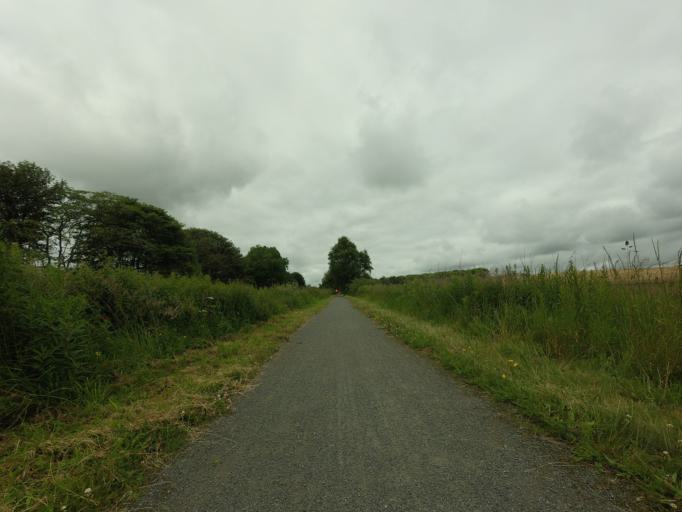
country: GB
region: Scotland
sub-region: Aberdeenshire
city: Ellon
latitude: 57.4773
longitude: -2.1295
